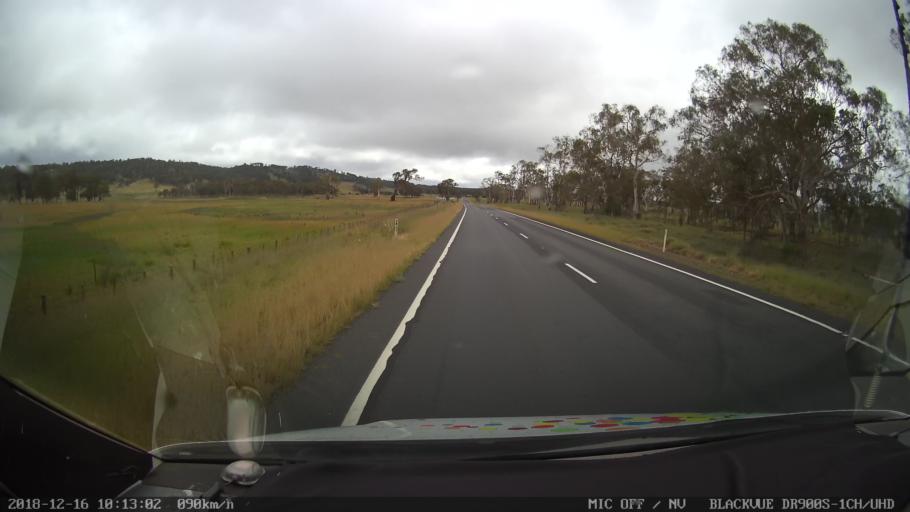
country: AU
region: New South Wales
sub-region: Glen Innes Severn
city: Glen Innes
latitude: -29.3008
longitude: 151.9481
